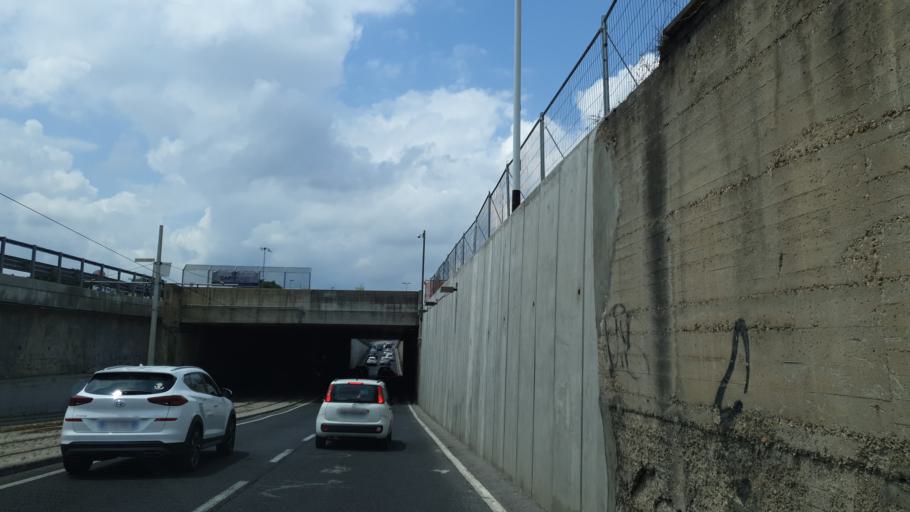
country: IT
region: Tuscany
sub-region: Province of Florence
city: Scandicci
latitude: 43.7733
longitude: 11.2138
